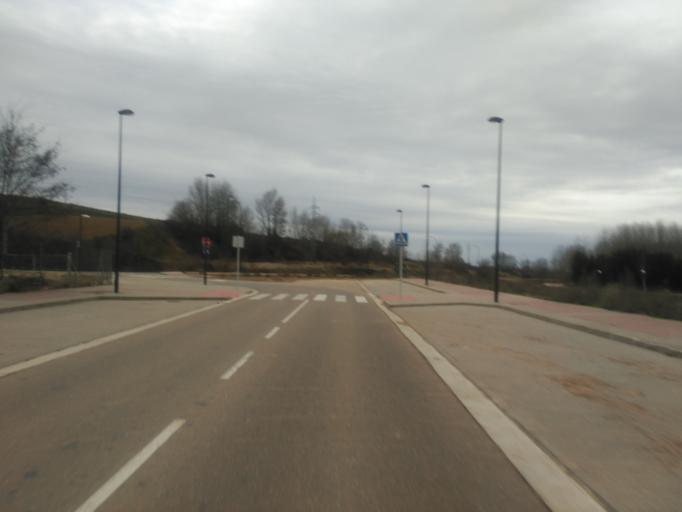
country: ES
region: Castille and Leon
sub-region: Provincia de Burgos
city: Villagonzalo-Pedernales
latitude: 42.3343
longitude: -3.7214
